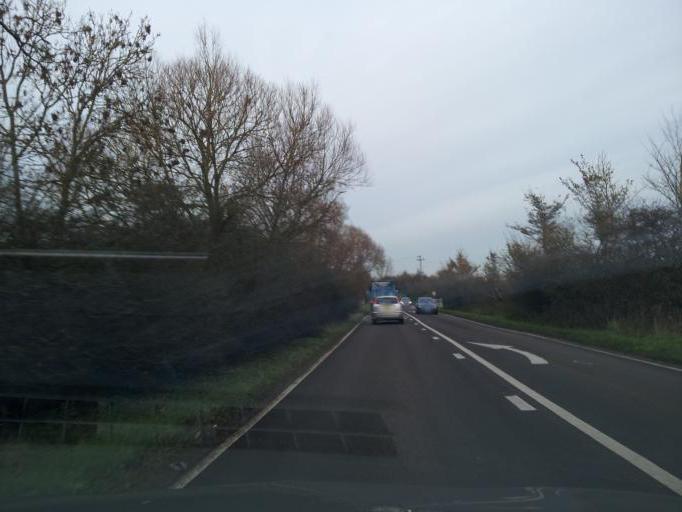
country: GB
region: England
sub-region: Buckinghamshire
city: Aylesbury
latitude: 51.8512
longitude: -0.7717
